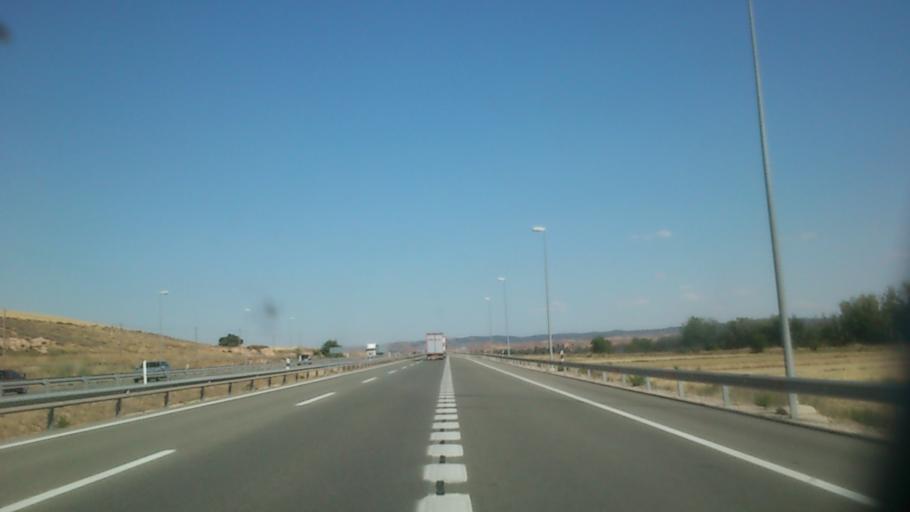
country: ES
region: Aragon
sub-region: Provincia de Zaragoza
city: Cetina
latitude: 41.3099
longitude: -1.9964
